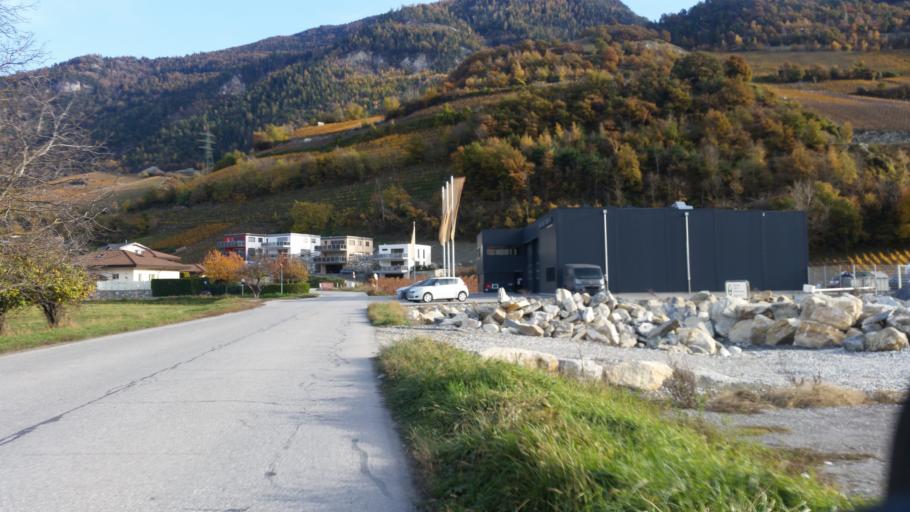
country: CH
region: Valais
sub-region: Sierre District
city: Chalais
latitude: 46.2606
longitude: 7.4851
